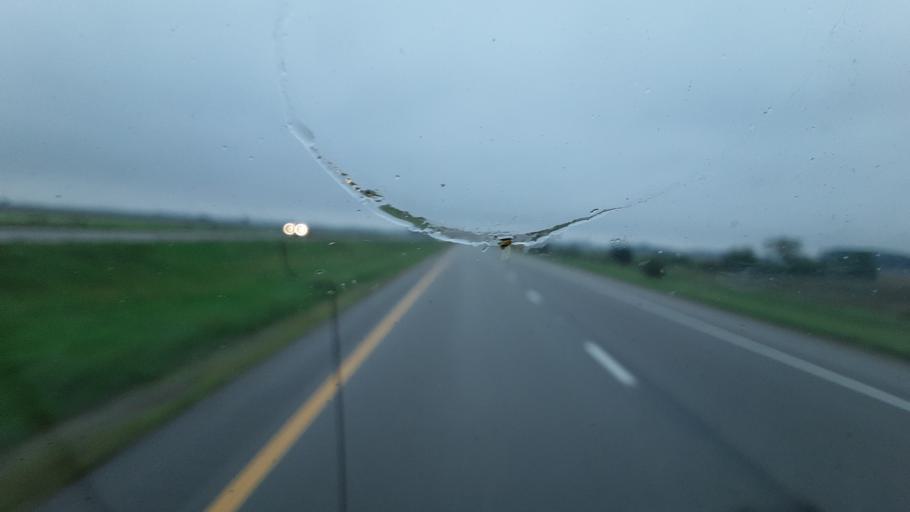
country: US
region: Ohio
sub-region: Van Wert County
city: Convoy
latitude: 40.9626
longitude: -84.7426
